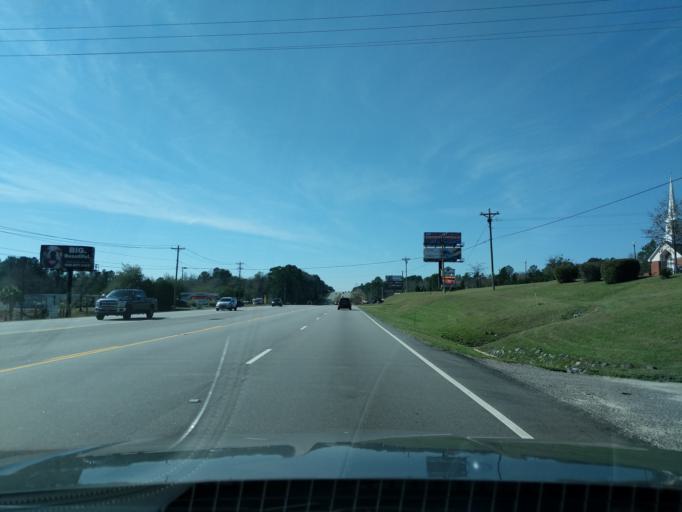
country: US
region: South Carolina
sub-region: Aiken County
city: Gloverville
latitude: 33.5399
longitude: -81.8307
